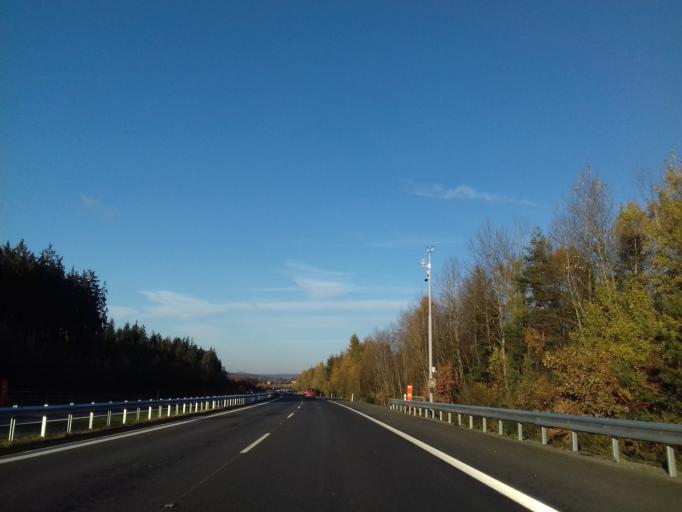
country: CZ
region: Plzensky
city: Myto
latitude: 49.8052
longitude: 13.7565
